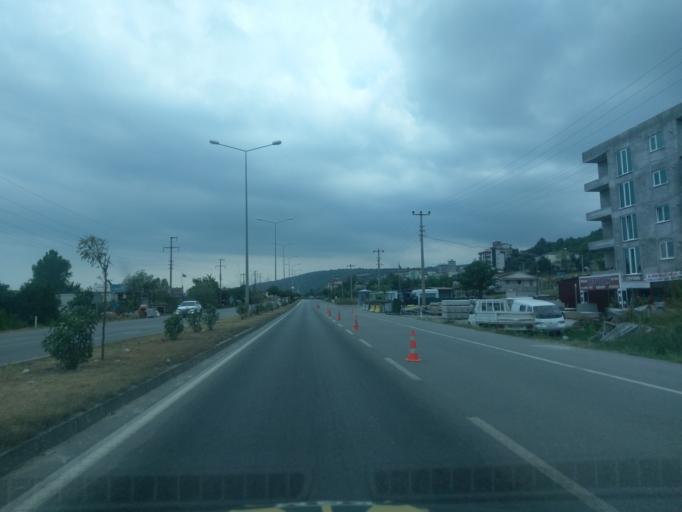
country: TR
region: Samsun
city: Taflan
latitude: 41.4136
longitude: 36.1743
